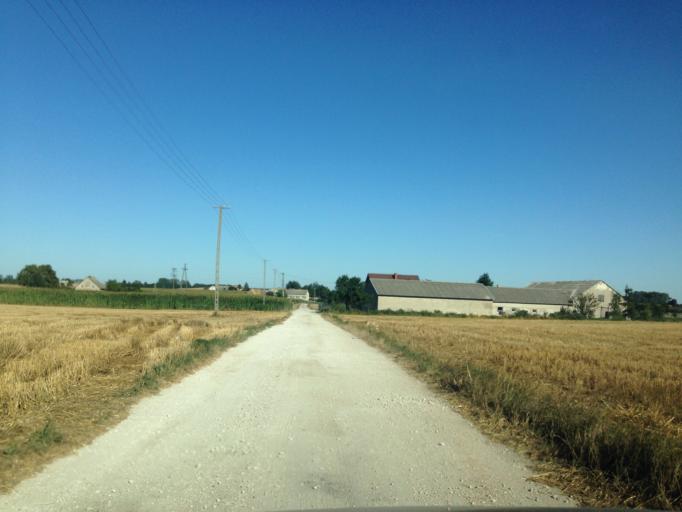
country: PL
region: Kujawsko-Pomorskie
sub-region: Powiat brodnicki
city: Swiedziebnia
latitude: 53.1894
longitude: 19.5808
